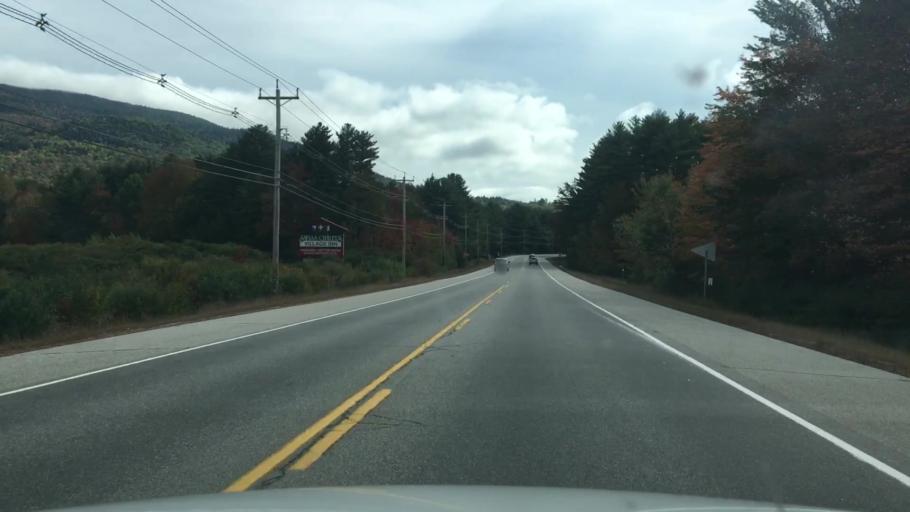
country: US
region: New Hampshire
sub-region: Carroll County
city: North Conway
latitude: 44.1053
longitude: -71.1571
